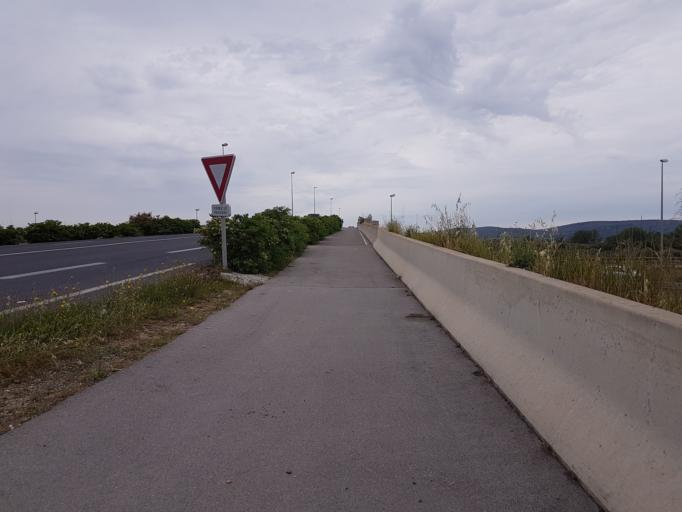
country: FR
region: Languedoc-Roussillon
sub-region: Departement de l'Herault
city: Frontignan
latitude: 43.4362
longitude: 3.7636
